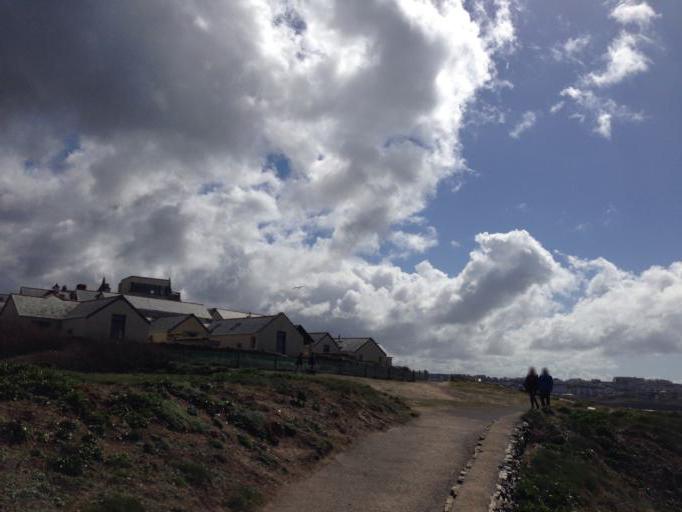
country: GB
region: England
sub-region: Cornwall
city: Newquay
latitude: 50.4226
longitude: -5.0974
